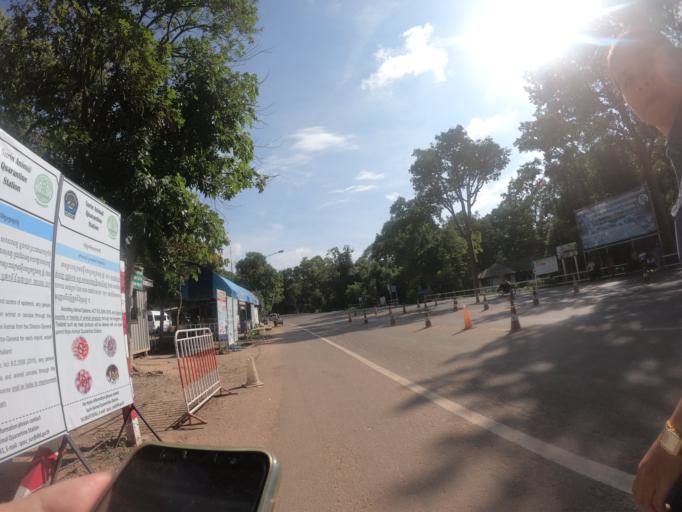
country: TH
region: Surin
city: Kap Choeng
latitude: 14.4357
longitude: 103.7003
